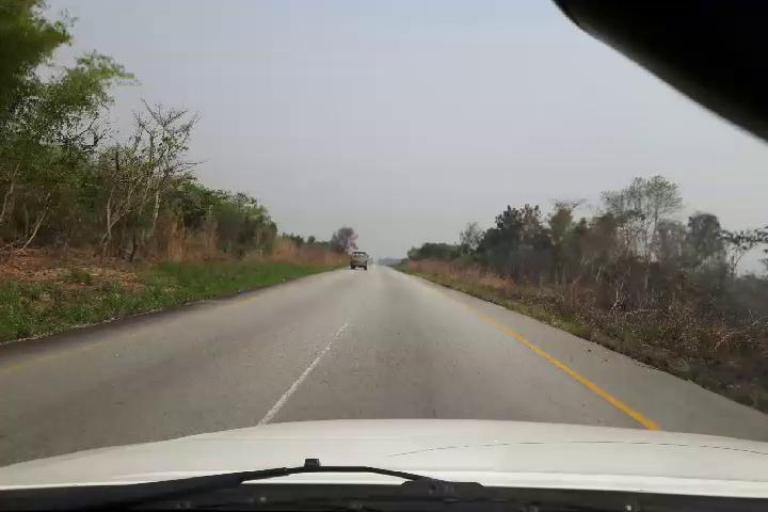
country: SL
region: Southern Province
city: Largo
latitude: 8.2420
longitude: -12.0859
